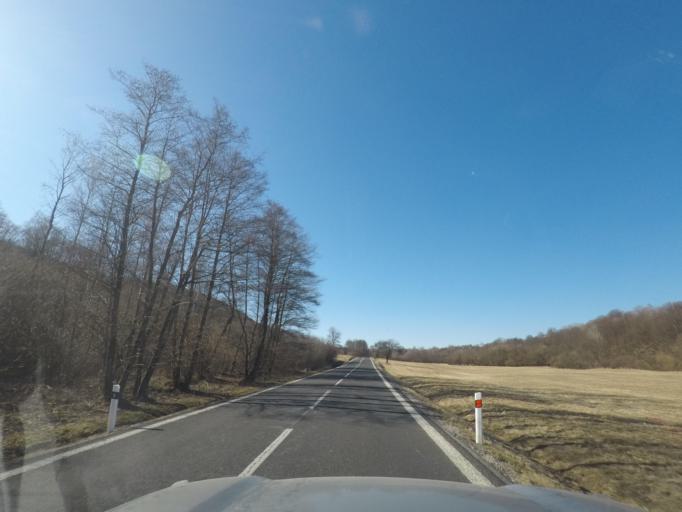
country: UA
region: Zakarpattia
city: Velykyi Bereznyi
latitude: 48.9180
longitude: 22.3603
